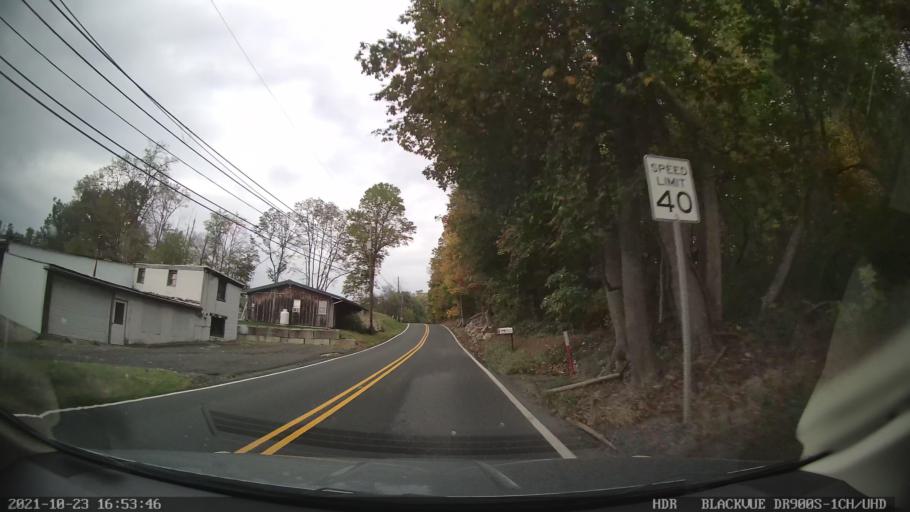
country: US
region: Pennsylvania
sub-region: Berks County
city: Red Lion
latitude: 40.4564
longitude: -75.5837
